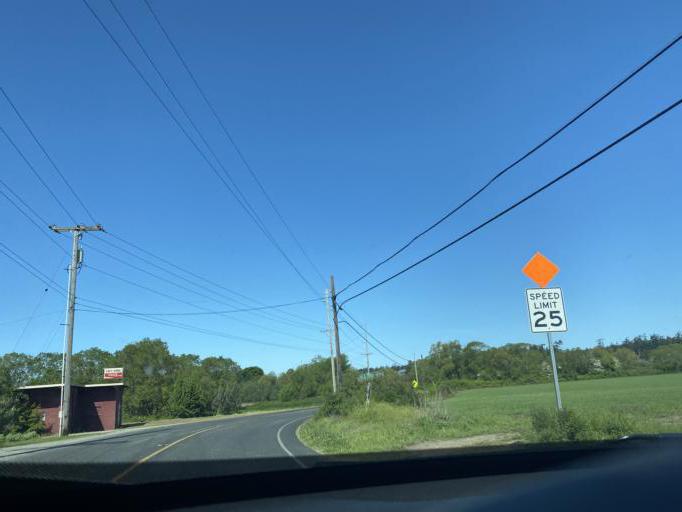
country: US
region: Washington
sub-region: Island County
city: Coupeville
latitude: 48.2067
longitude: -122.6804
